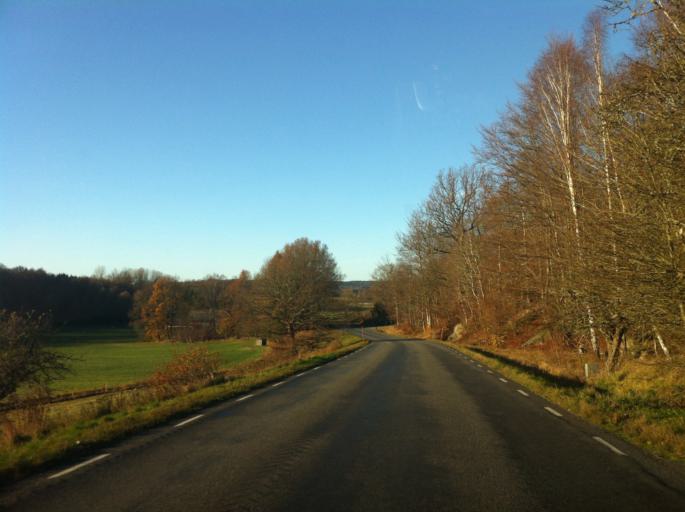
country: SE
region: Blekinge
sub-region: Olofstroms Kommun
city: Jamshog
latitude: 56.1807
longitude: 14.5651
